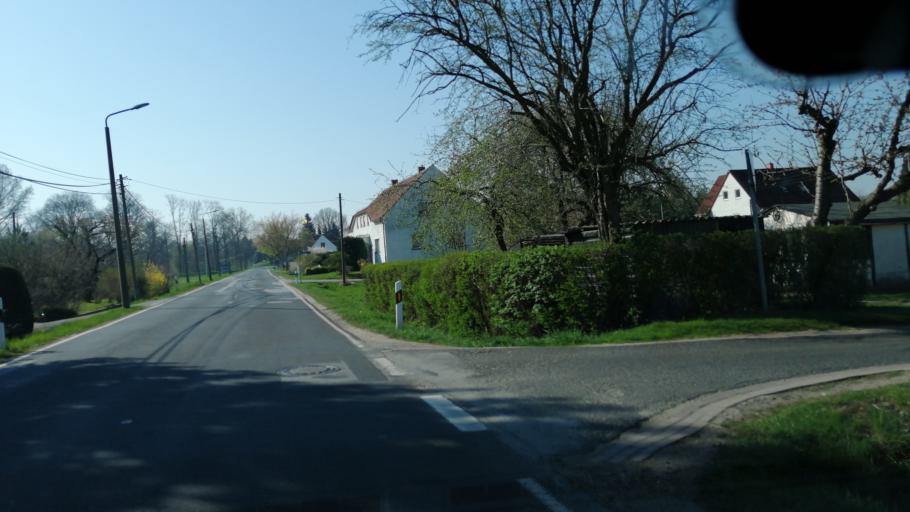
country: DE
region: Saxony
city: Goerlitz
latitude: 51.1729
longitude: 14.9348
